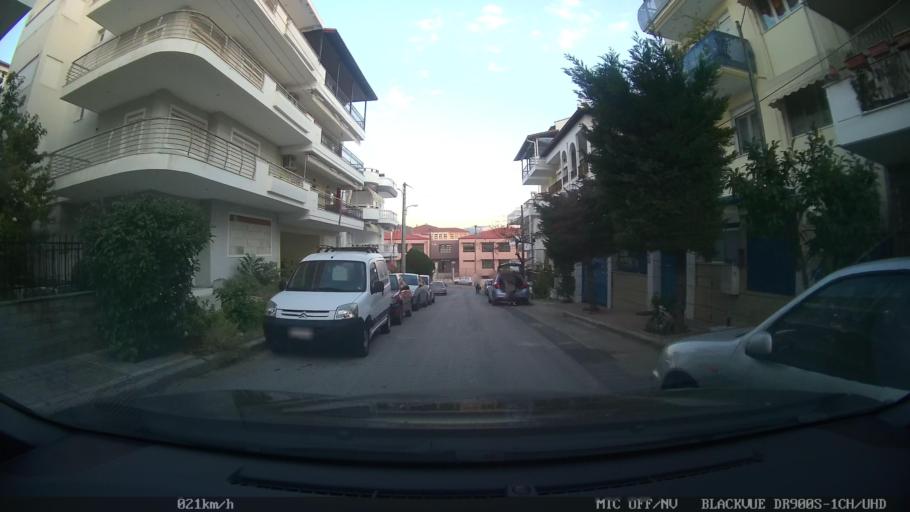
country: GR
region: Central Macedonia
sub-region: Nomos Thessalonikis
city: Pylaia
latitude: 40.6124
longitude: 22.9931
